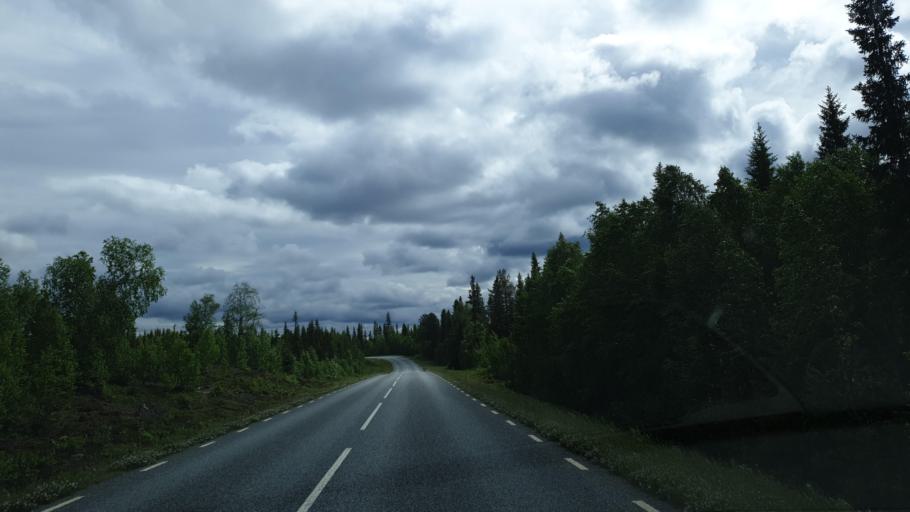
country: SE
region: Vaesterbotten
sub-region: Vilhelmina Kommun
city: Sjoberg
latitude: 65.2319
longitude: 15.8641
